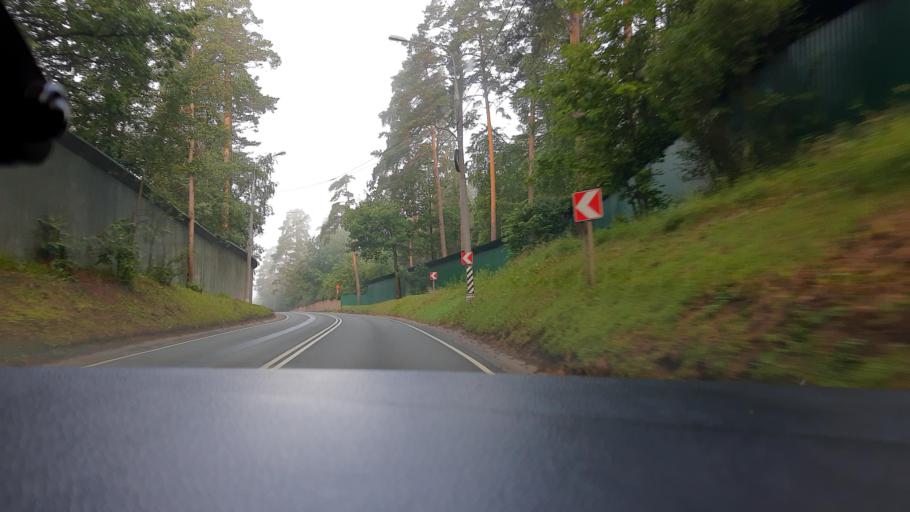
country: RU
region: Moskovskaya
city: Nikolina Gora
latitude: 55.7066
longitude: 37.0417
